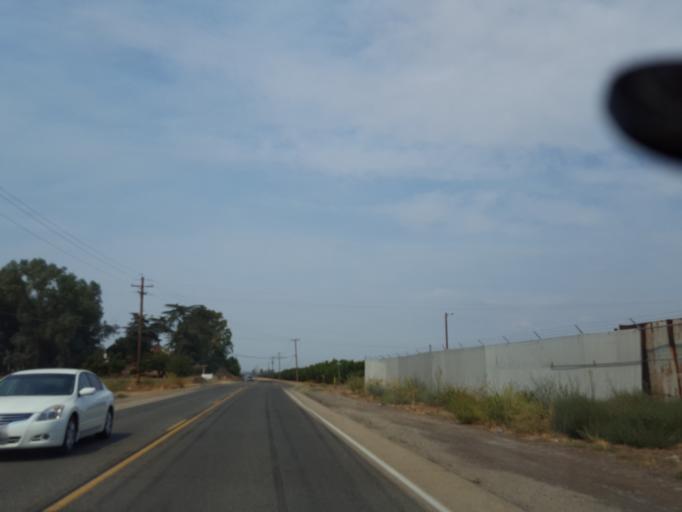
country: US
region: California
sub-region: Fresno County
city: Minkler
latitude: 36.6760
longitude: -119.4575
